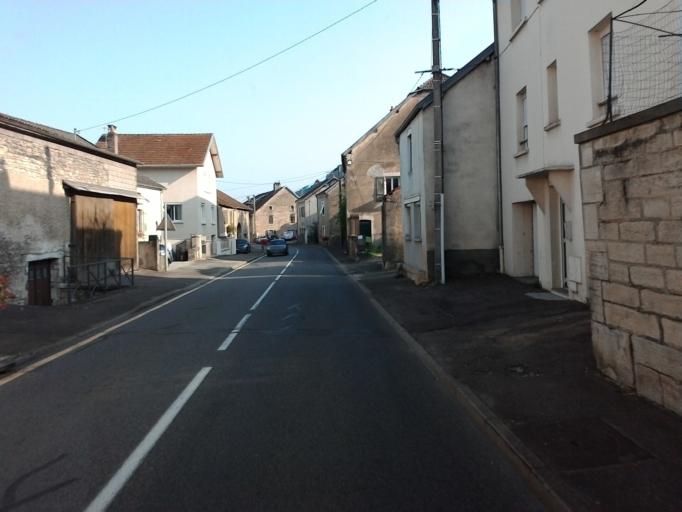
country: FR
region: Franche-Comte
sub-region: Departement de la Haute-Saone
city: Frotey-les-Vesoul
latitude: 47.6219
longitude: 6.1841
